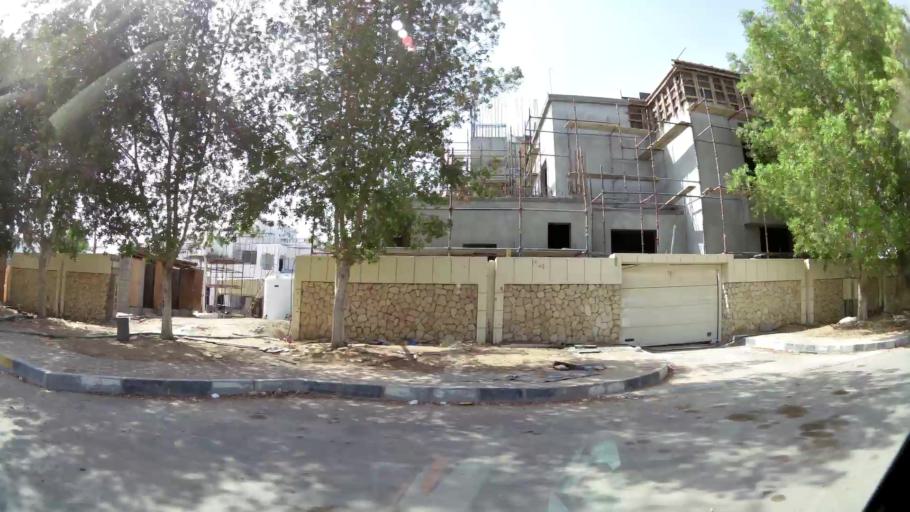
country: AE
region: Abu Dhabi
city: Al Ain
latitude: 24.2255
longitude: 55.6845
